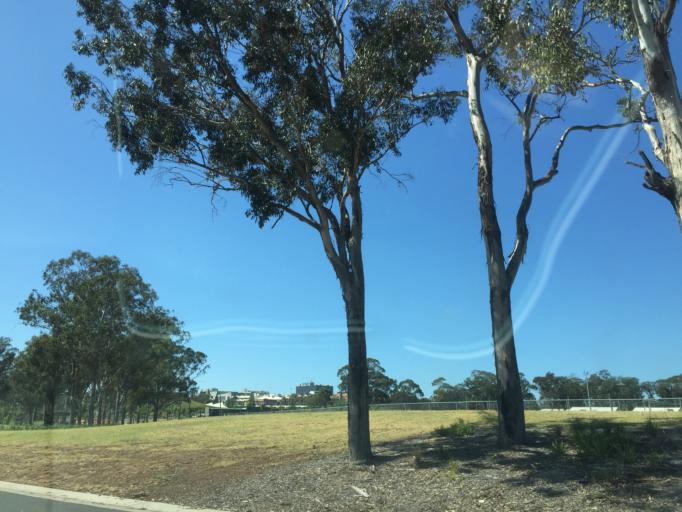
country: AU
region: New South Wales
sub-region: Blacktown
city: Blacktown
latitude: -33.7643
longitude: 150.9005
